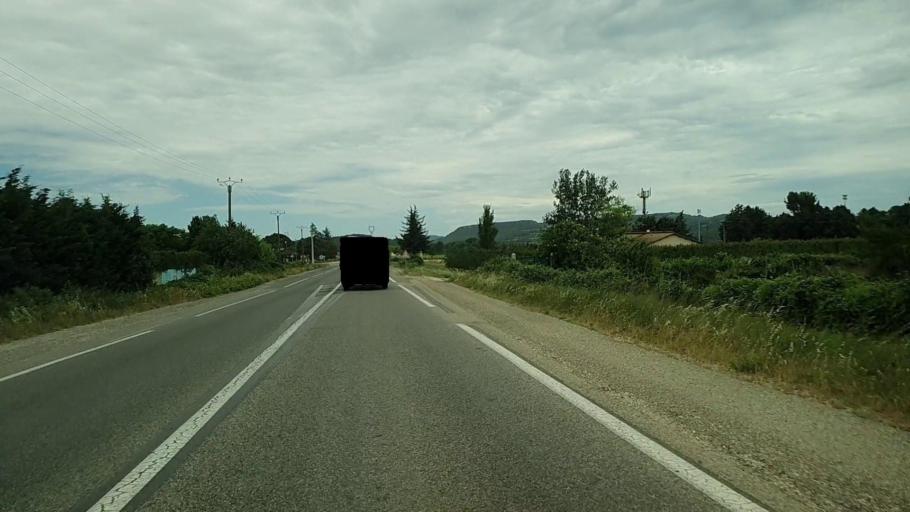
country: FR
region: Languedoc-Roussillon
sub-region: Departement du Gard
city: Connaux
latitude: 44.0856
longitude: 4.5941
